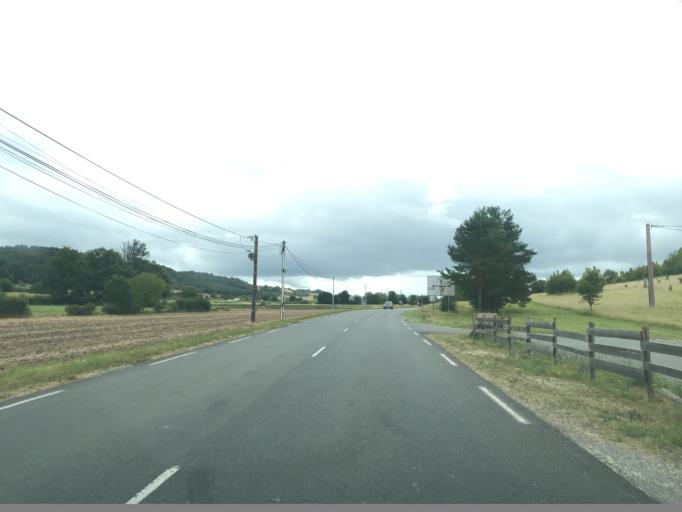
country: FR
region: Aquitaine
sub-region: Departement de la Dordogne
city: Brantome
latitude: 45.4066
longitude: 0.5874
